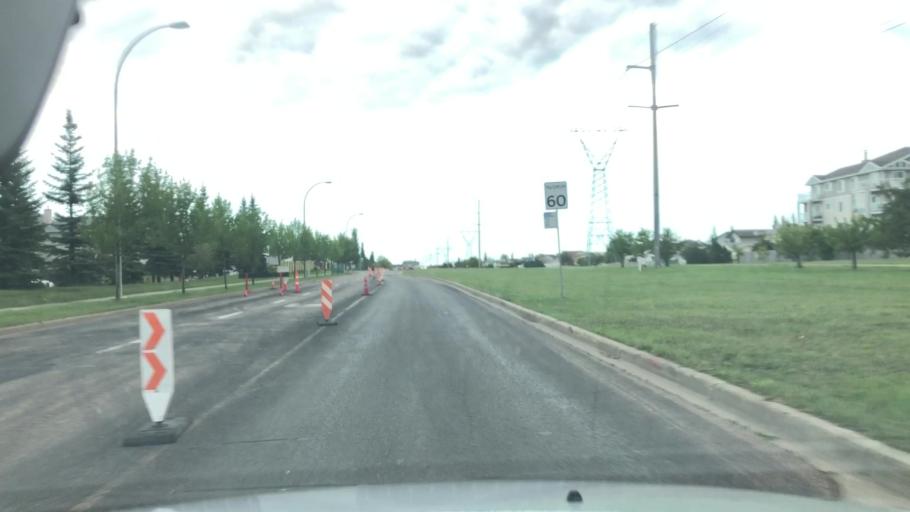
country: CA
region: Alberta
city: St. Albert
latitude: 53.6146
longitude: -113.5598
